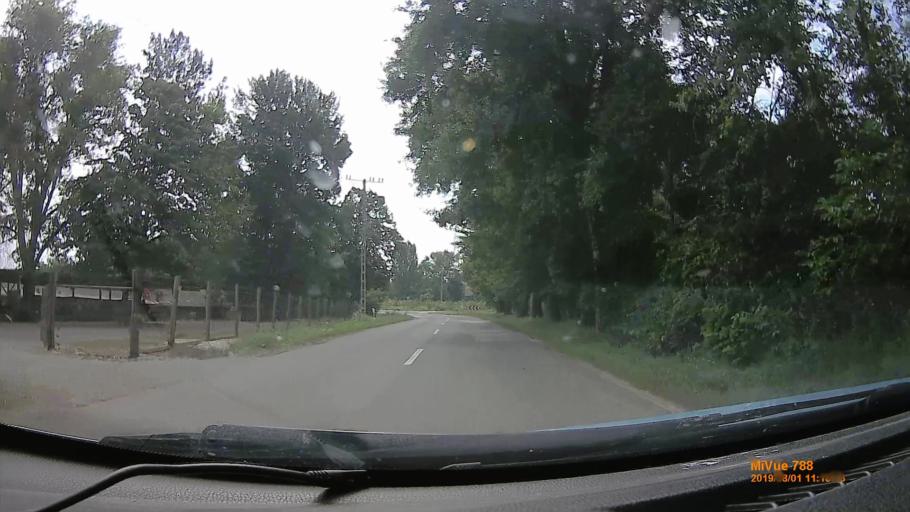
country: HU
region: Baranya
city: Pellerd
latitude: 46.0106
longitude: 18.2106
